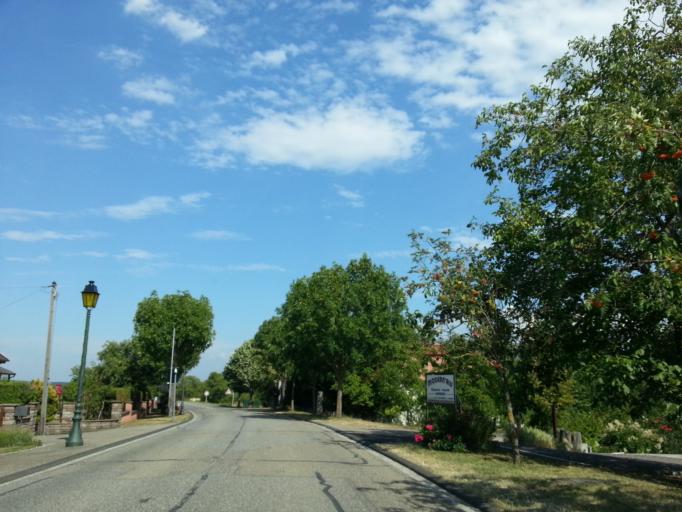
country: FR
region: Alsace
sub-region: Departement du Bas-Rhin
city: Goersdorf
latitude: 48.9362
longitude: 7.7792
